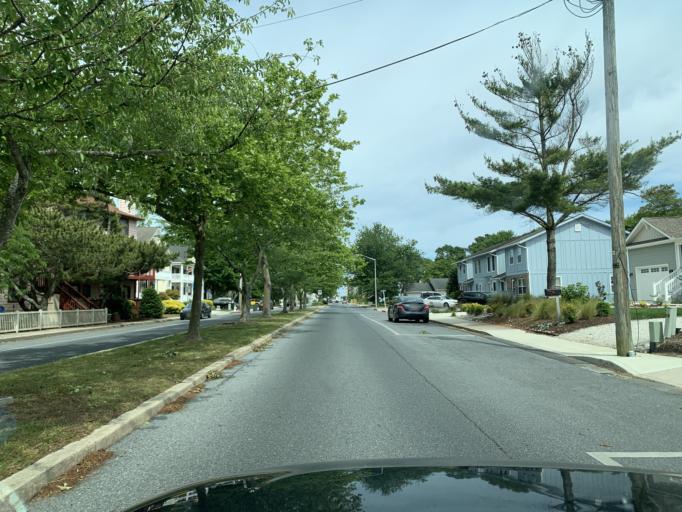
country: US
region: Delaware
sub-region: Sussex County
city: Bethany Beach
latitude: 38.4476
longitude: -75.0564
